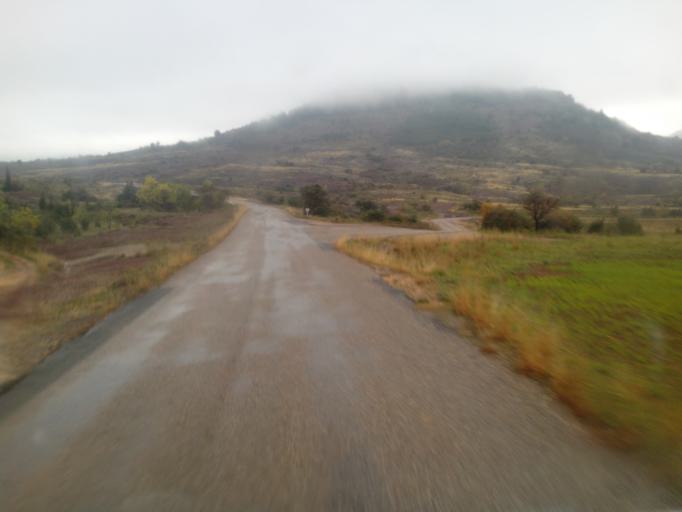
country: FR
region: Languedoc-Roussillon
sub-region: Departement de l'Herault
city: Lodeve
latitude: 43.6459
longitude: 3.3507
